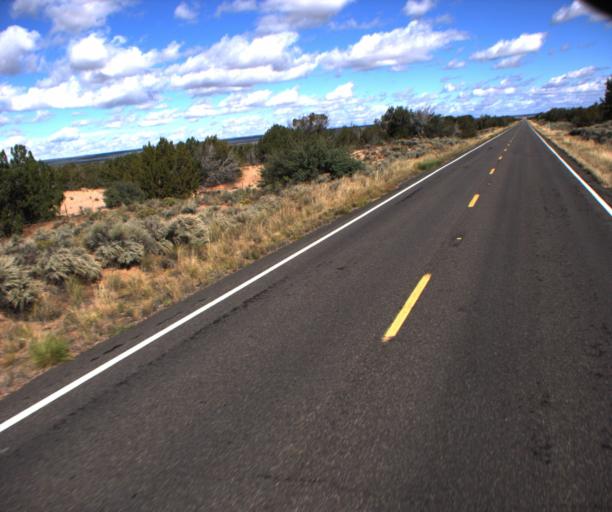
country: US
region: Arizona
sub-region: Apache County
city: Saint Johns
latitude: 34.8636
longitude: -109.2377
